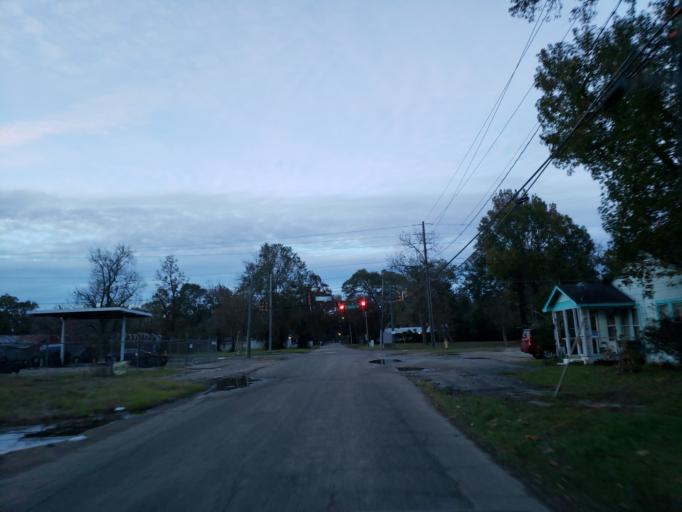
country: US
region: Mississippi
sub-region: Forrest County
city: Hattiesburg
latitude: 31.3245
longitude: -89.2801
